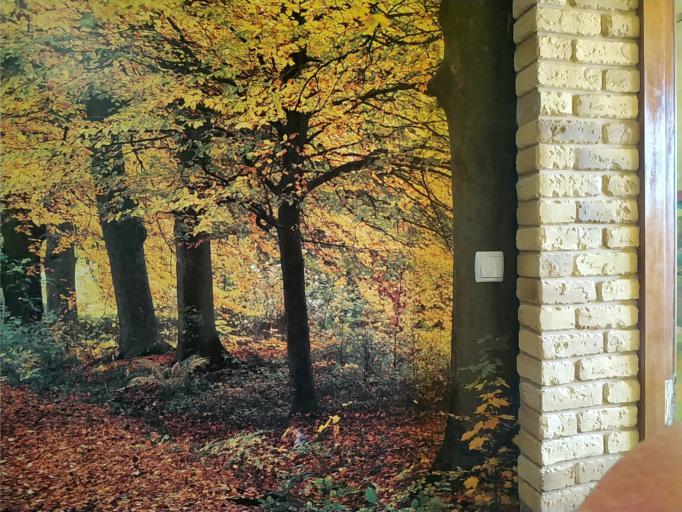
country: RU
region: Vologda
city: Nelazskoye
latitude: 59.4663
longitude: 37.6058
